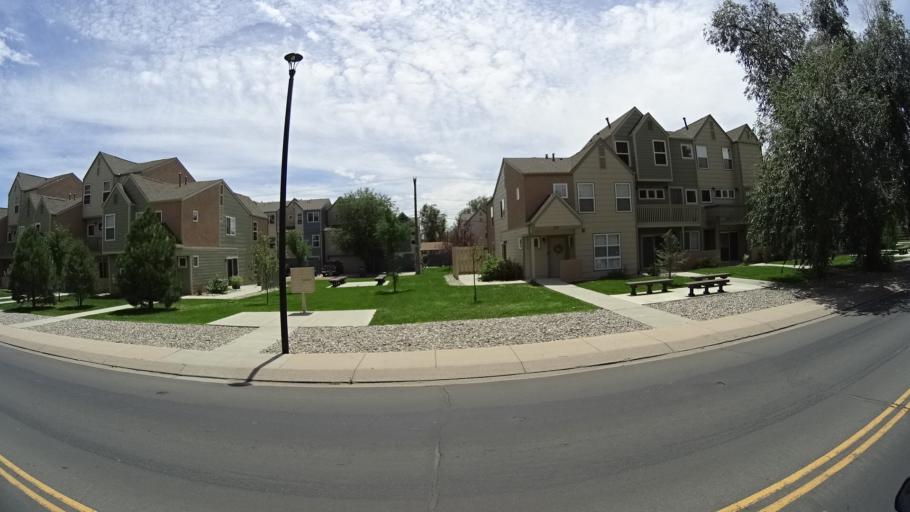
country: US
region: Colorado
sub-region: El Paso County
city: Fountain
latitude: 38.6832
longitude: -104.6974
